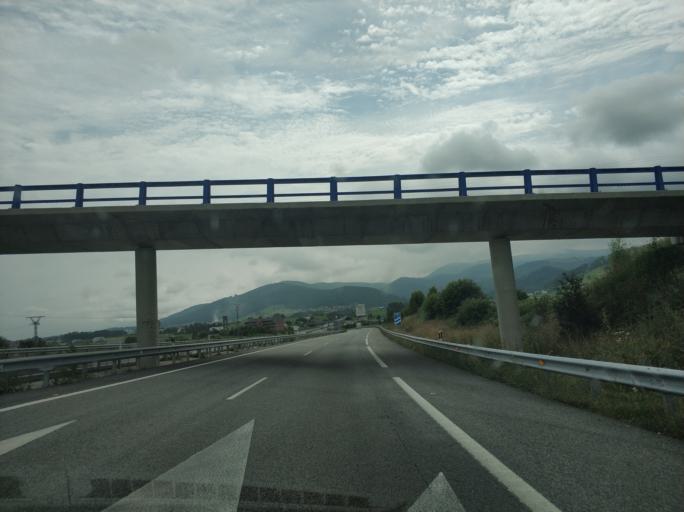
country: ES
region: Asturias
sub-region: Province of Asturias
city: Navia
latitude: 43.5291
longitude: -6.5611
